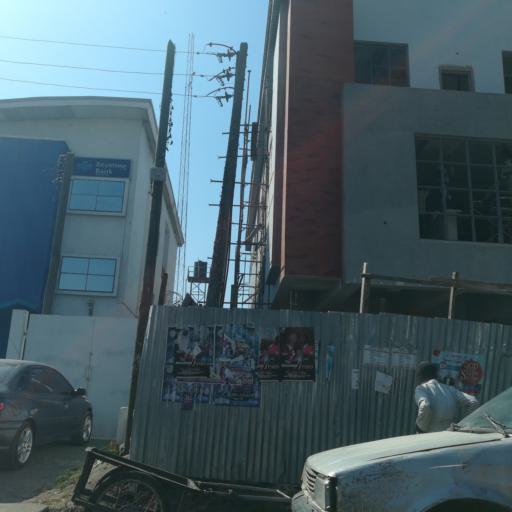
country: NG
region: Kano
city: Kano
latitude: 12.0143
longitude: 8.5329
